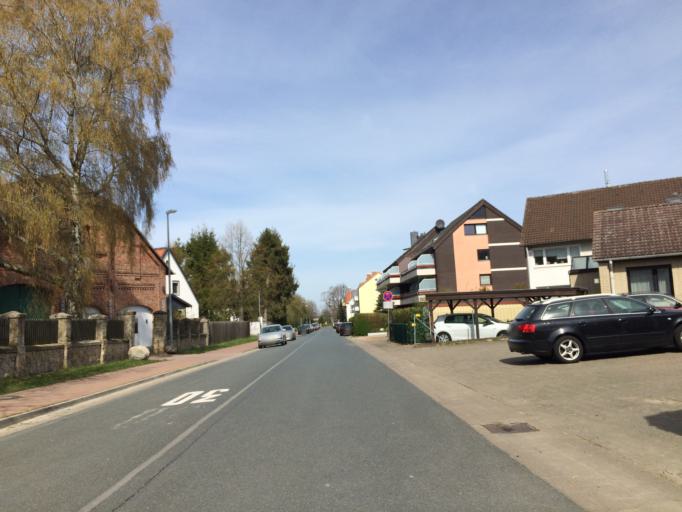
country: DE
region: Lower Saxony
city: Gehrden
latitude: 52.3176
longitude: 9.5984
